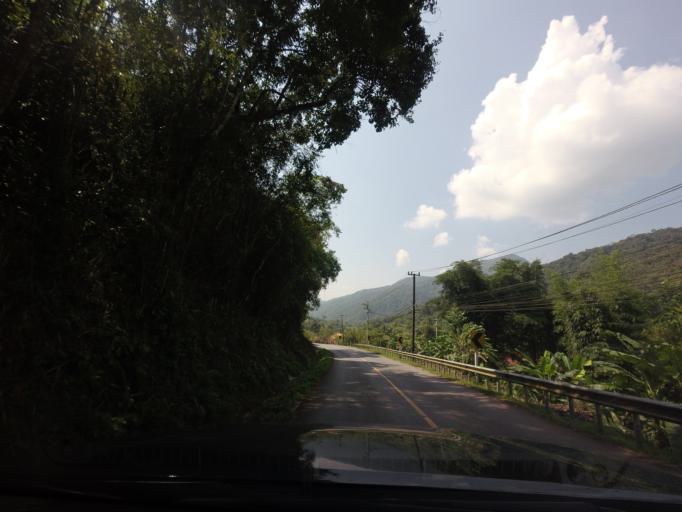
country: TH
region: Nan
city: Bo Kluea
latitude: 19.1395
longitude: 101.1516
